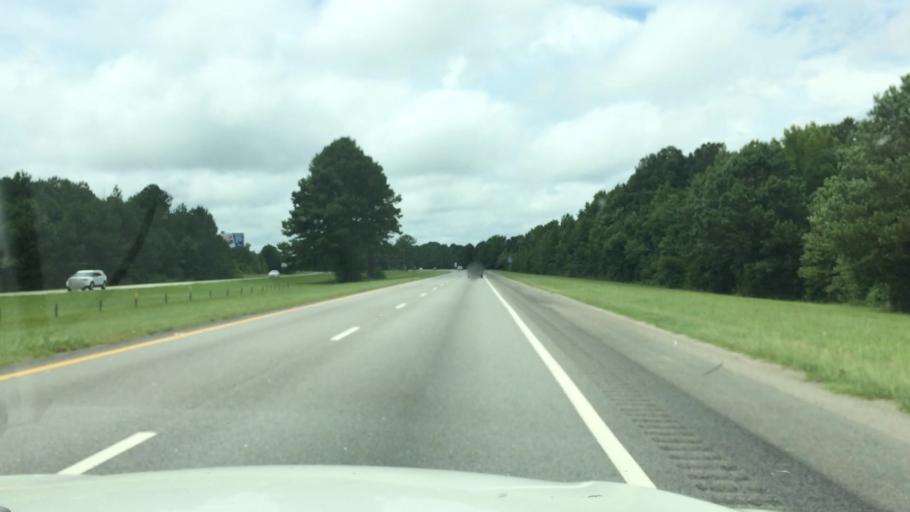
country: US
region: South Carolina
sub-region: Florence County
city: Timmonsville
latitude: 34.2063
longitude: -79.9214
